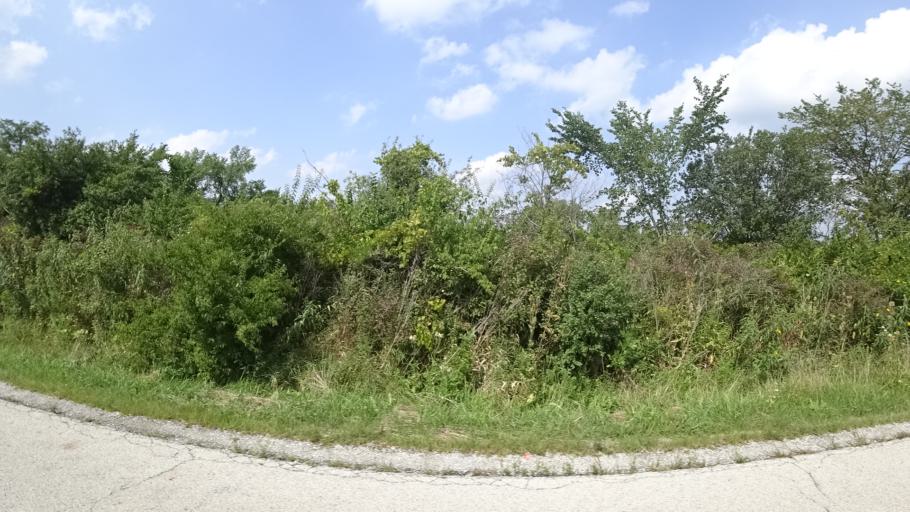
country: US
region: Illinois
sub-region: Cook County
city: Orland Park
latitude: 41.6443
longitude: -87.8900
